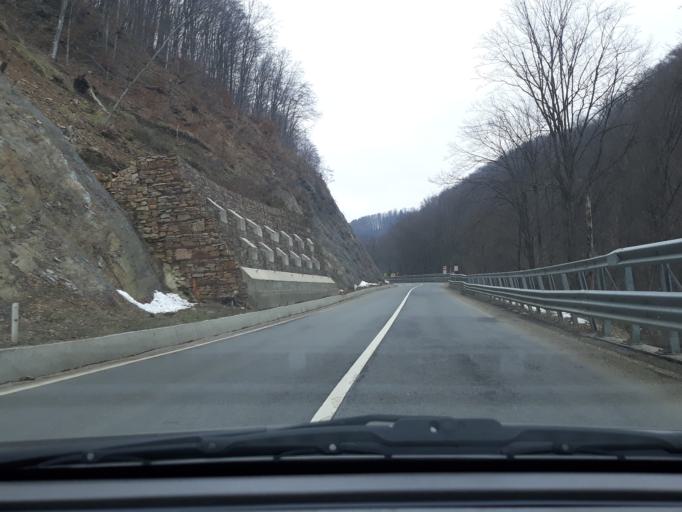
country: RO
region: Bihor
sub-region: Oras Alesd
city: Padurea Neagra
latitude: 47.1199
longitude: 22.4105
